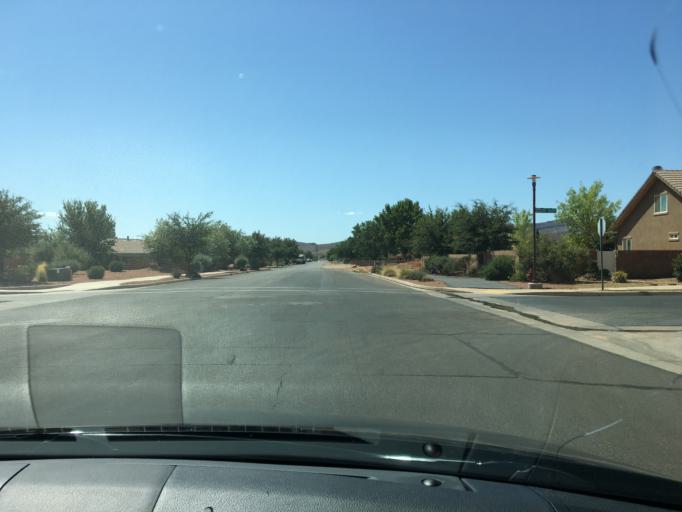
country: US
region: Utah
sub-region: Washington County
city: Ivins
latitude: 37.1651
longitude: -113.6888
